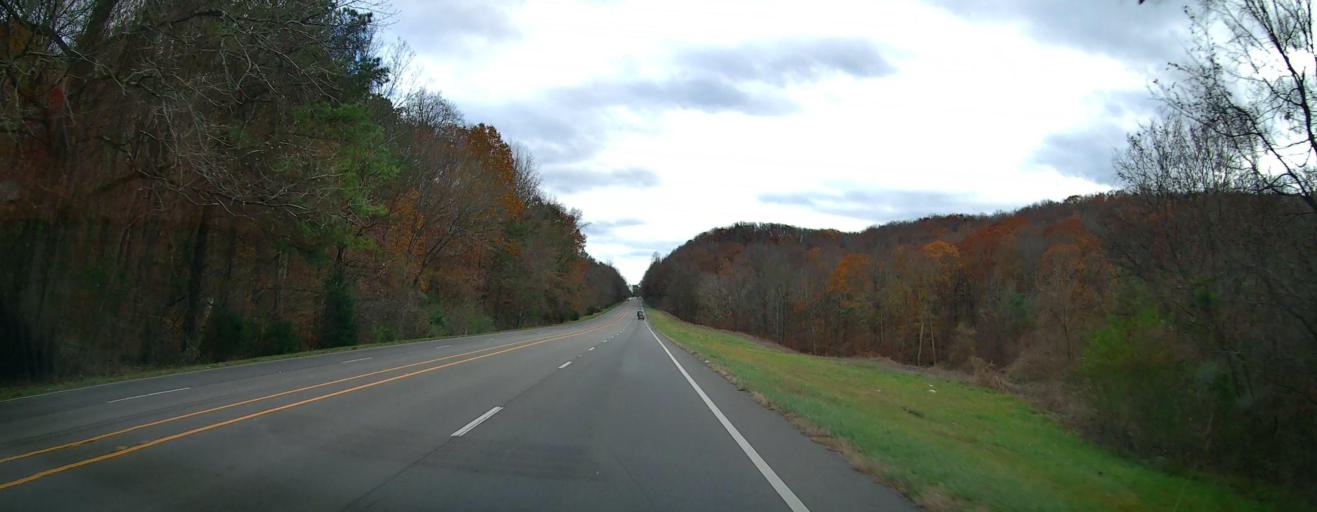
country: US
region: Alabama
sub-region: Morgan County
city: Falkville
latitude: 34.3186
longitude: -87.0001
